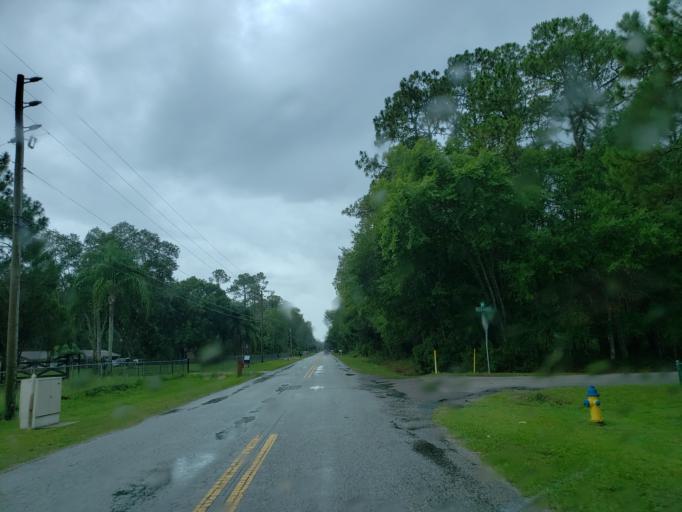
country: US
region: Florida
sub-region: Pasco County
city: Wesley Chapel
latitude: 28.2714
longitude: -82.3531
